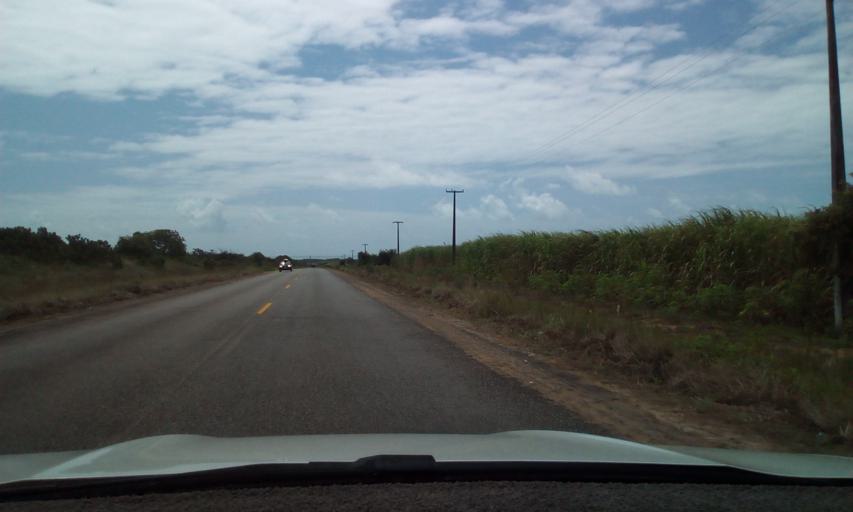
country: BR
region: Paraiba
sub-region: Rio Tinto
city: Rio Tinto
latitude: -6.7456
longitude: -34.9703
